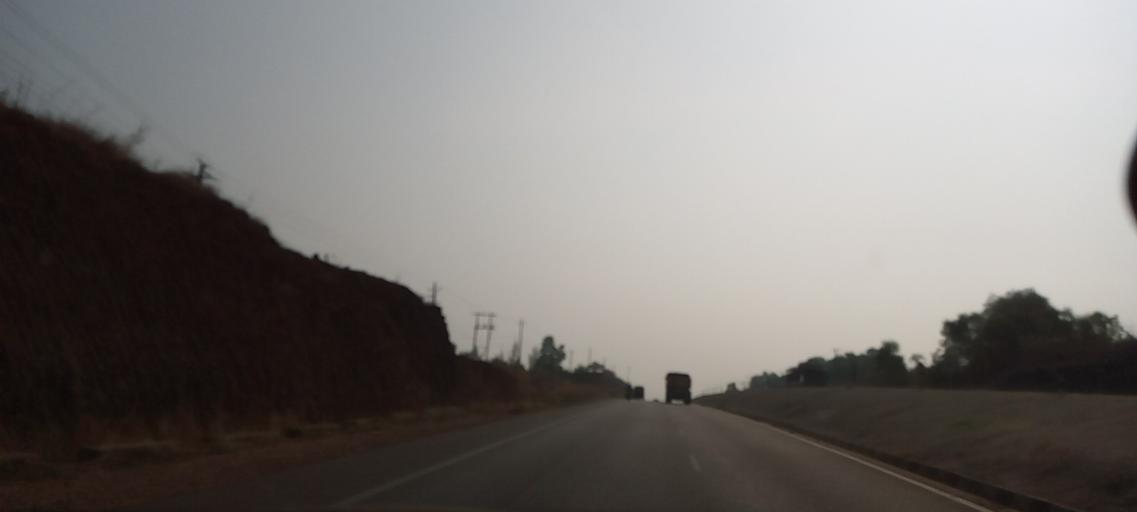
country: IN
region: Karnataka
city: Gangolli
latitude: 13.6885
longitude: 74.6678
